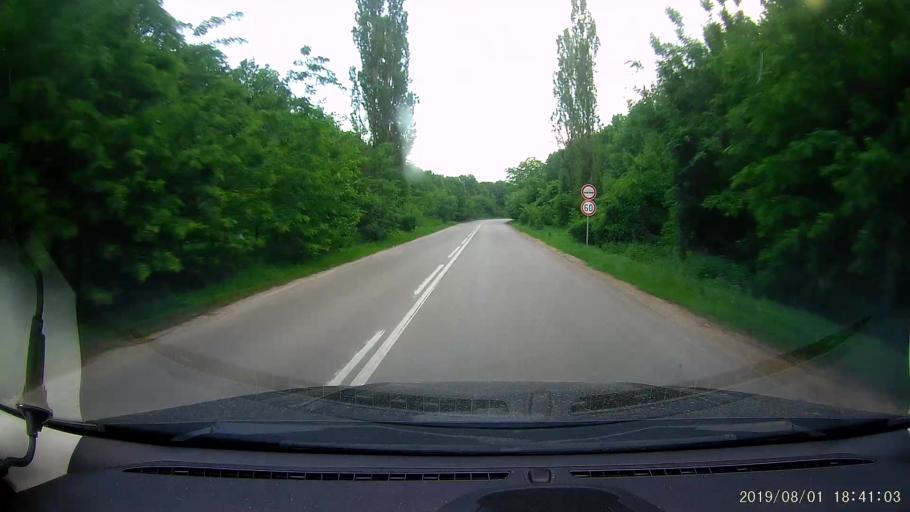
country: BG
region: Shumen
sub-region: Obshtina Khitrino
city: Gara Khitrino
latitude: 43.3528
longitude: 26.9233
